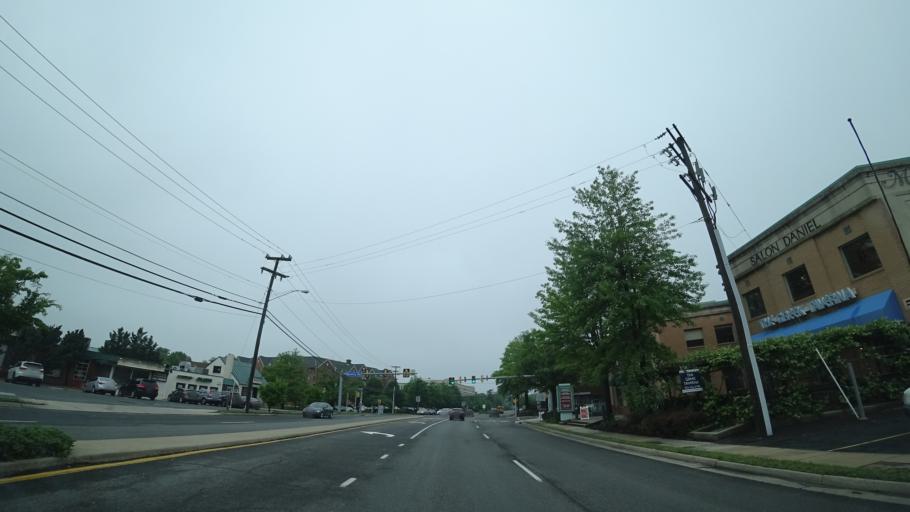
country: US
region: Virginia
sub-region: Fairfax County
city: McLean
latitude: 38.9345
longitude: -77.1792
